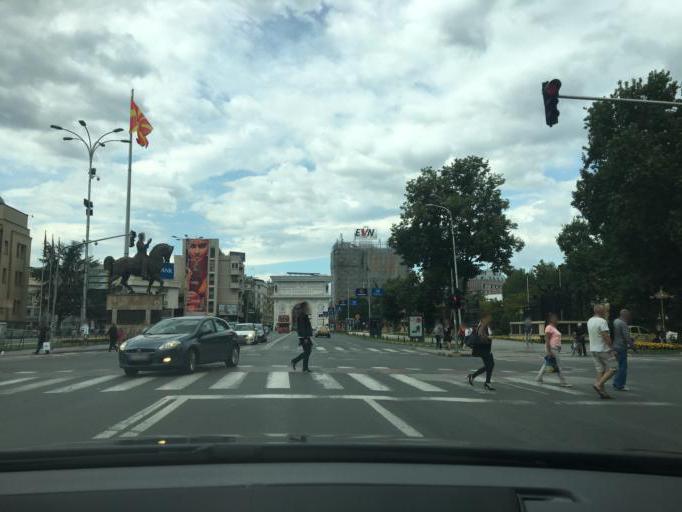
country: MK
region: Karpos
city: Skopje
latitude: 41.9926
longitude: 21.4338
